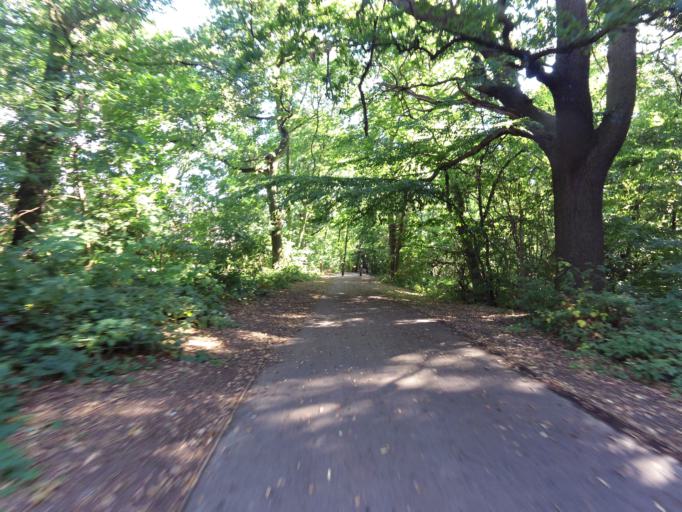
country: GB
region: England
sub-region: Greater London
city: Wood Green
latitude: 51.6272
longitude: -0.1420
